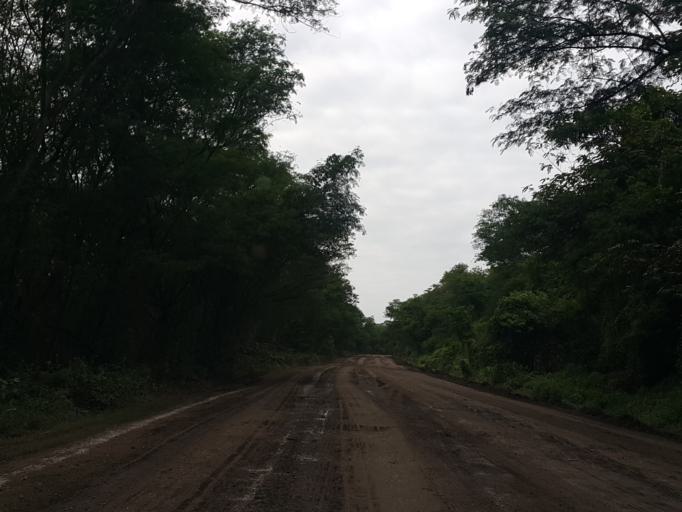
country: TH
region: Lampang
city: Mae Mo
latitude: 18.3135
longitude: 99.7508
